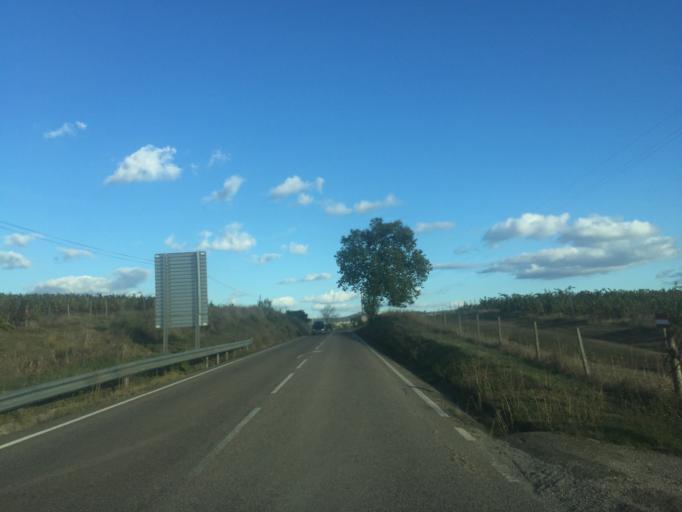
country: PT
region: Portalegre
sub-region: Alter do Chao
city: Alter do Chao
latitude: 39.1957
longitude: -7.6903
